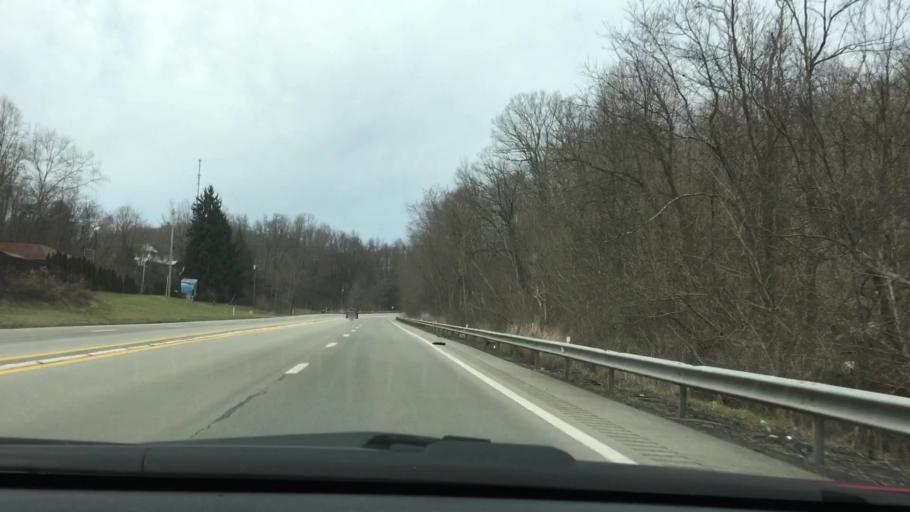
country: US
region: Pennsylvania
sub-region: Fayette County
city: Perryopolis
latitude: 40.0105
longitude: -79.7645
